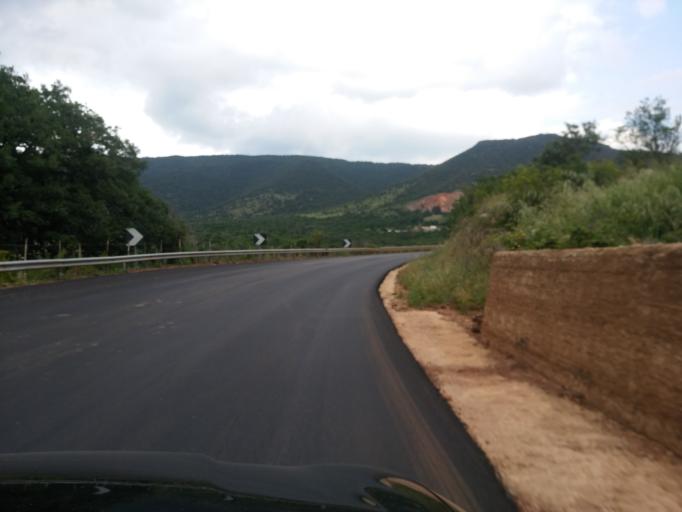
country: IT
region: Apulia
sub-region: Provincia di Foggia
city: Rignano Garganico
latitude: 41.7189
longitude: 15.5663
